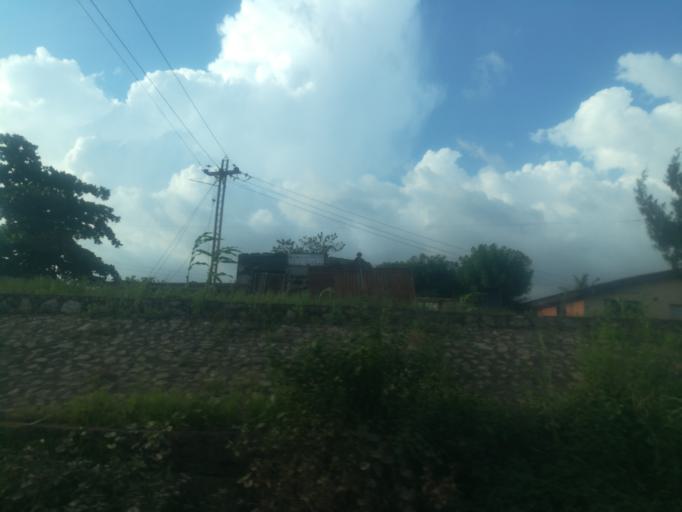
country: NG
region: Oyo
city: Ibadan
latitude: 7.3825
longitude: 3.8707
